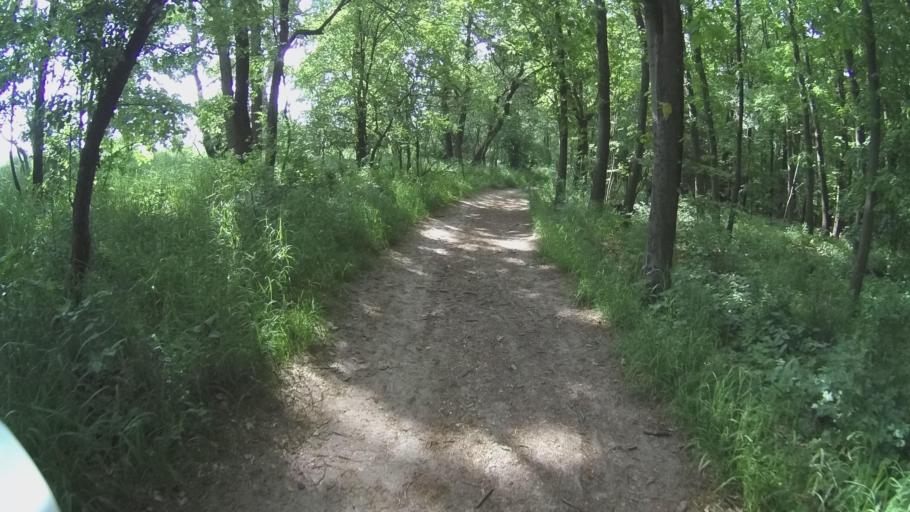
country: CZ
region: Central Bohemia
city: Zdiby
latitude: 50.1968
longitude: 14.4471
